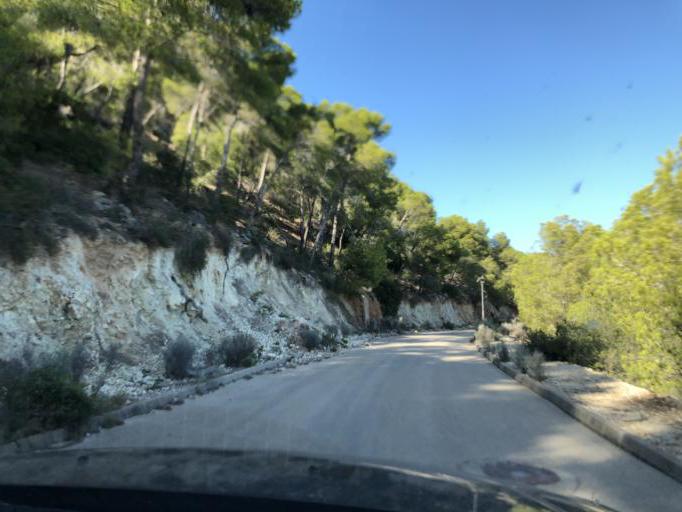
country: ES
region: Balearic Islands
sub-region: Illes Balears
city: Camp de Mar
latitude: 39.5374
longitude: 2.4045
